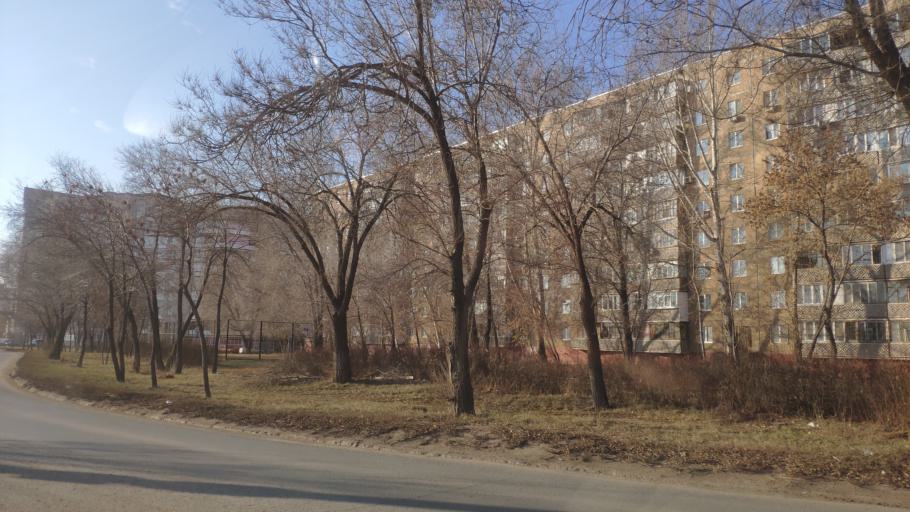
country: RU
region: Orenburg
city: Prigorodnyy
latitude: 51.7764
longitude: 55.1921
